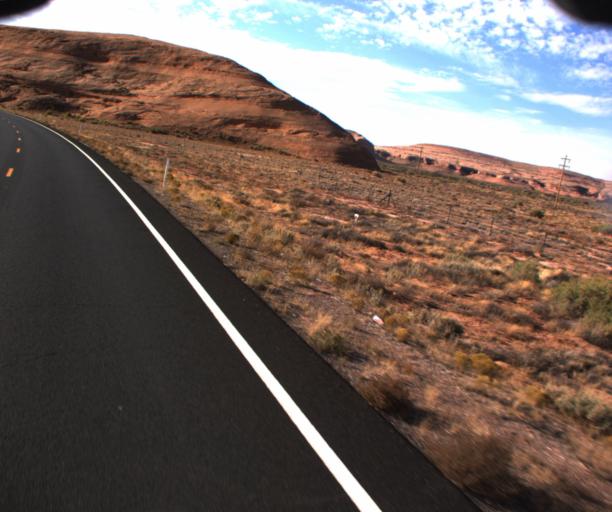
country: US
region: Arizona
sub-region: Apache County
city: Many Farms
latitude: 36.7738
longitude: -109.6614
